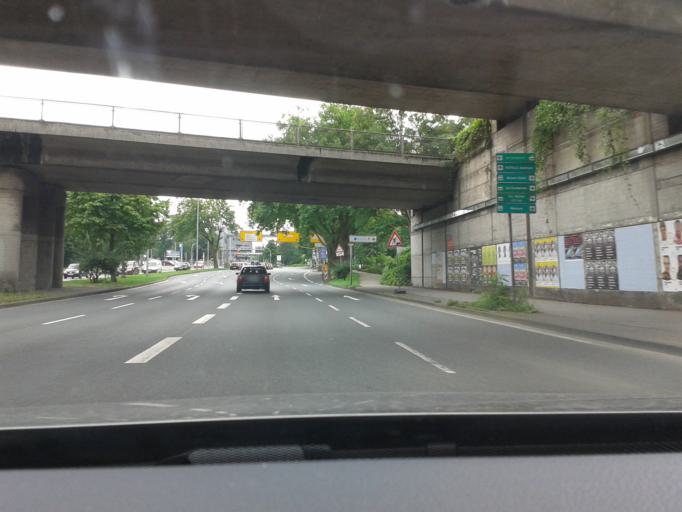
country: DE
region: North Rhine-Westphalia
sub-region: Regierungsbezirk Dusseldorf
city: Oberhausen
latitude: 51.4895
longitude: 6.8618
